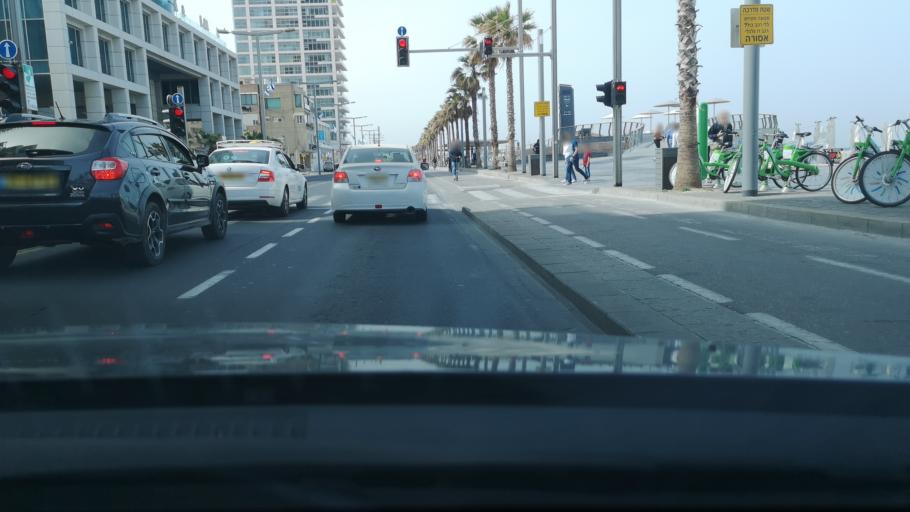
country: IL
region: Tel Aviv
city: Tel Aviv
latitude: 32.0711
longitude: 34.7640
